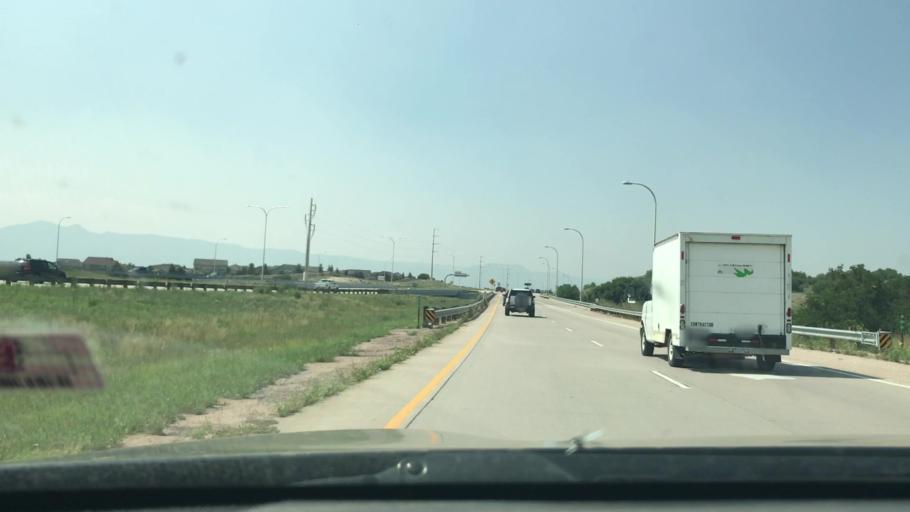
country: US
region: Colorado
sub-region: El Paso County
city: Black Forest
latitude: 38.9750
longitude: -104.7509
